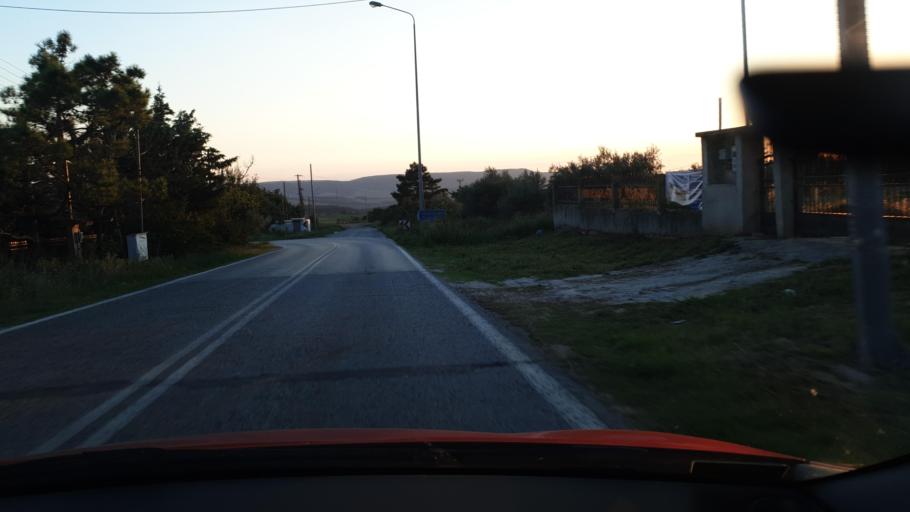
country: GR
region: Central Macedonia
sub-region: Nomos Chalkidikis
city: Galatista
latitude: 40.4685
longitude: 23.2502
